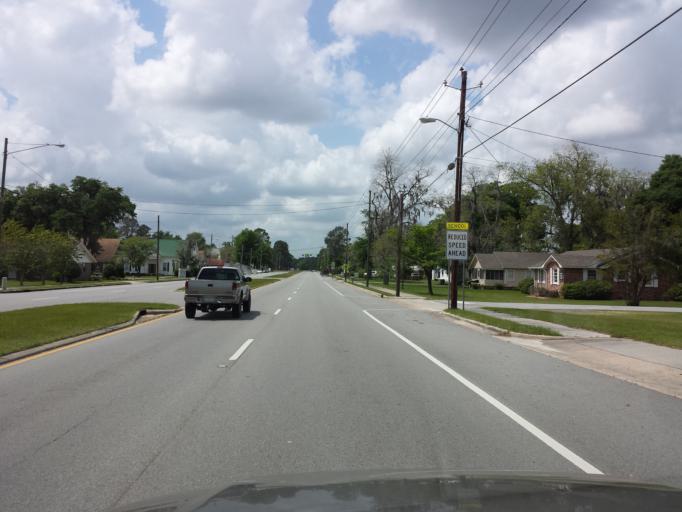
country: US
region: Georgia
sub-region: Echols County
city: Statenville
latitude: 30.6847
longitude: -83.1811
